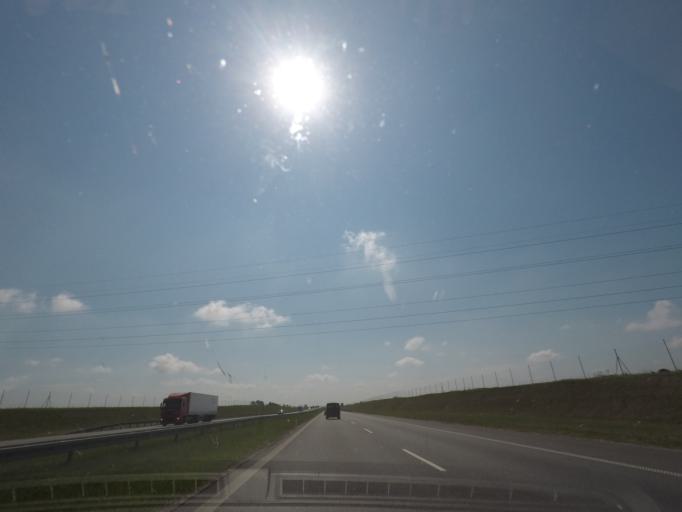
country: PL
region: Kujawsko-Pomorskie
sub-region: Powiat wloclawski
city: Czerniewice
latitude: 52.5526
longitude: 19.0393
